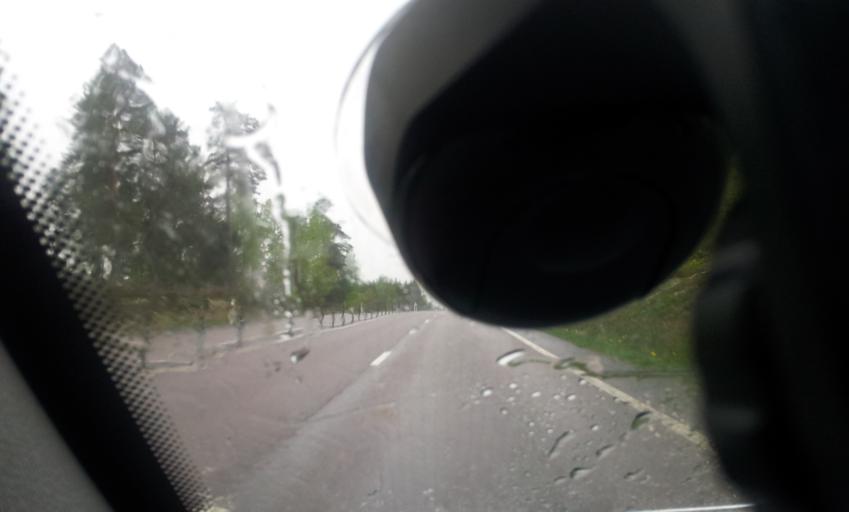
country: SE
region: Kalmar
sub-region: Oskarshamns Kommun
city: Oskarshamn
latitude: 57.4061
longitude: 16.4819
